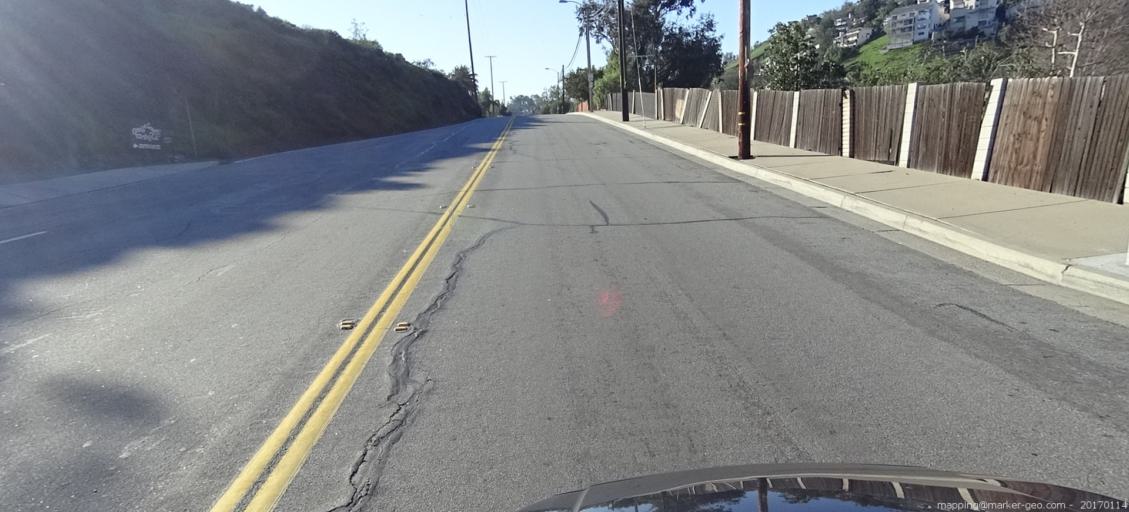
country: US
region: California
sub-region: Orange County
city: North Tustin
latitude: 33.7871
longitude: -117.7958
